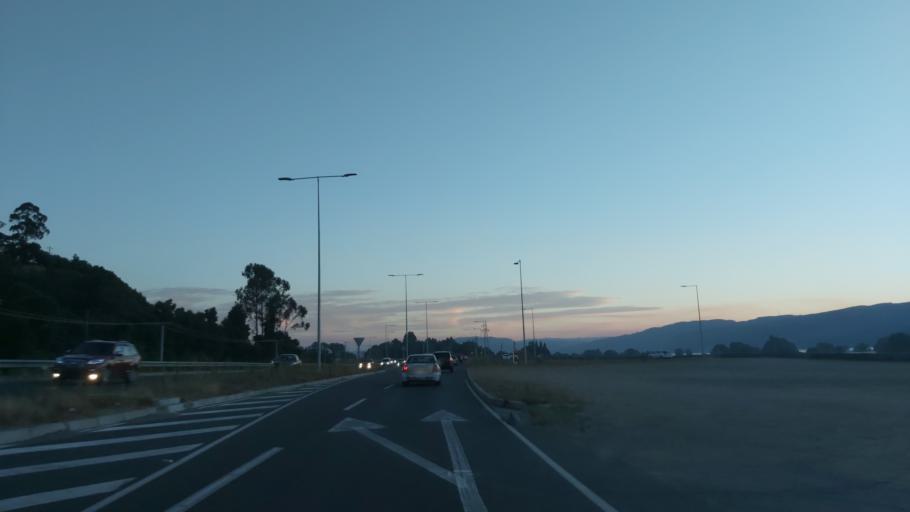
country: CL
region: Biobio
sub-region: Provincia de Concepcion
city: Chiguayante
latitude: -36.8902
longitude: -73.0369
